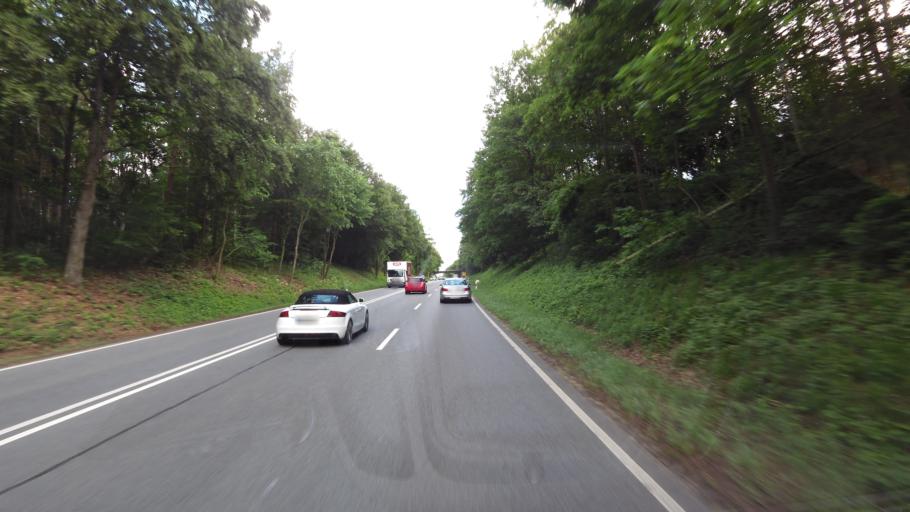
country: DE
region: Bavaria
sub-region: Upper Bavaria
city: Breitbrunn
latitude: 48.0275
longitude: 12.1743
